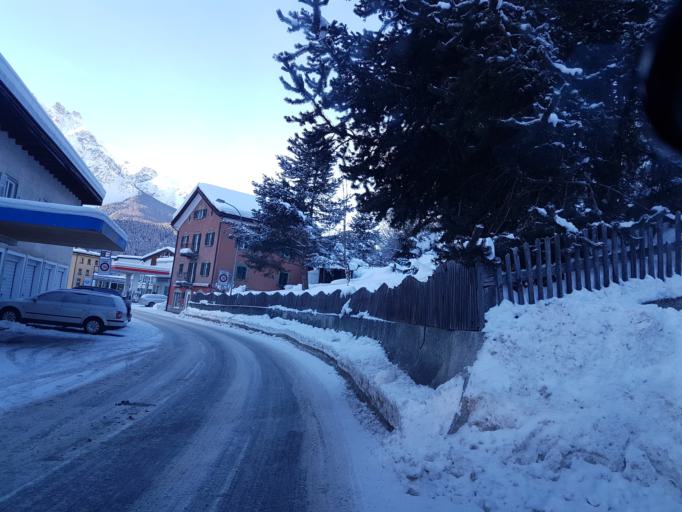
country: CH
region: Grisons
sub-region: Inn District
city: Scuol
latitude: 46.7993
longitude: 10.3050
